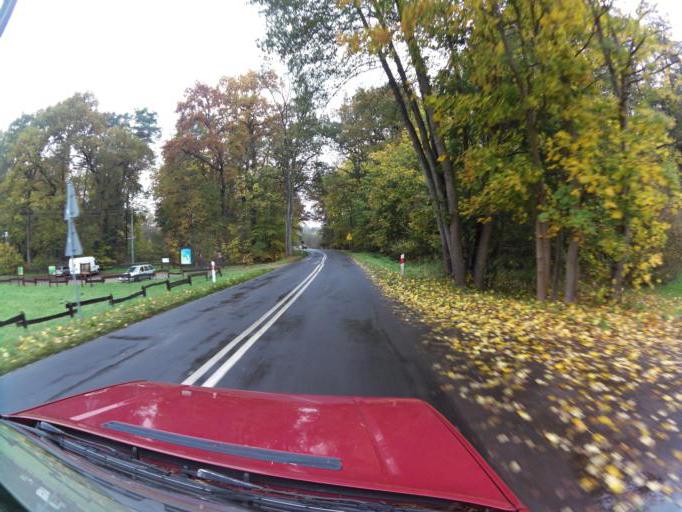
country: PL
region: West Pomeranian Voivodeship
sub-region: Powiat policki
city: Dobra
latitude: 53.5532
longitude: 14.4565
